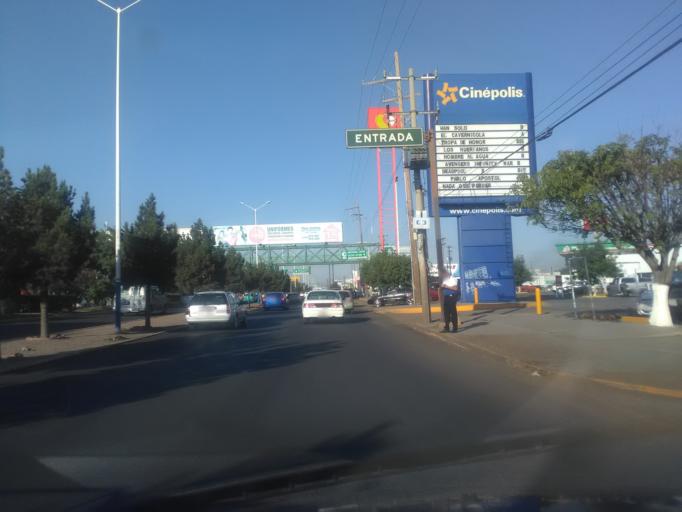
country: MX
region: Durango
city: Victoria de Durango
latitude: 24.0423
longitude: -104.6292
